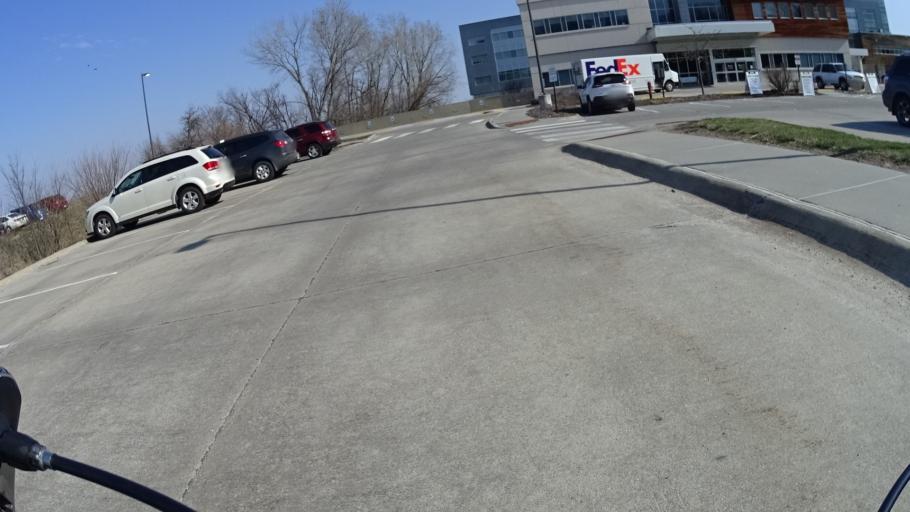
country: US
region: Nebraska
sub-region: Sarpy County
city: Offutt Air Force Base
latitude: 41.1364
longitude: -95.9489
